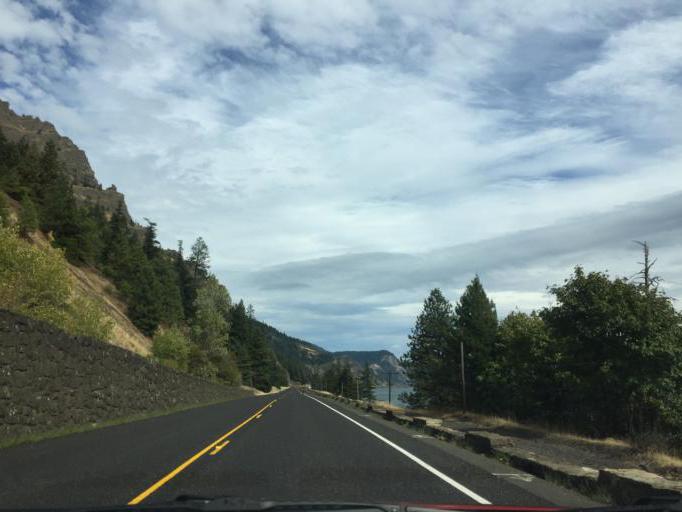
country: US
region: Washington
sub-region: Skamania County
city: Carson
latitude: 45.7004
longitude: -121.7009
